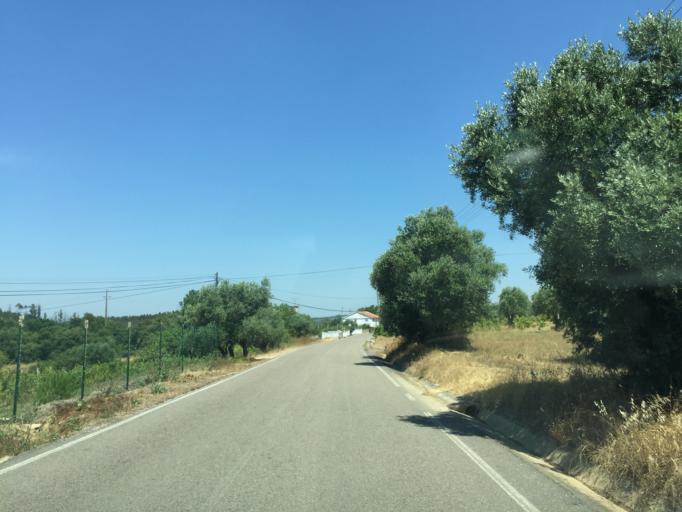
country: PT
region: Santarem
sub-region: Tomar
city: Tomar
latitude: 39.5868
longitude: -8.3274
